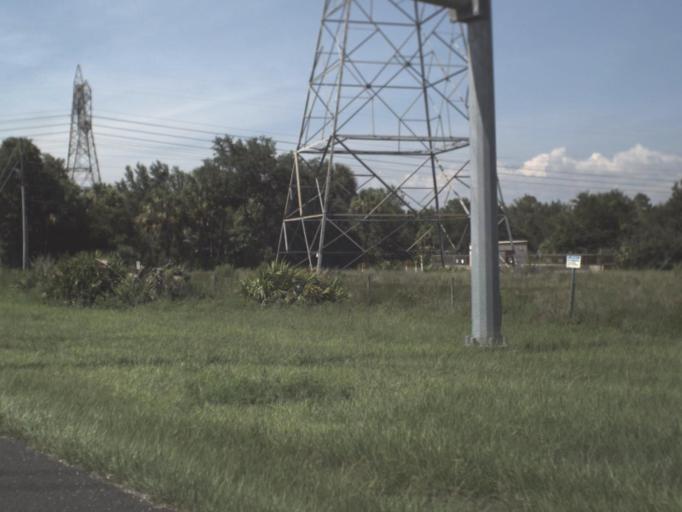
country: US
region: Florida
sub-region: Citrus County
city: Crystal River
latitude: 28.9596
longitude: -82.6301
